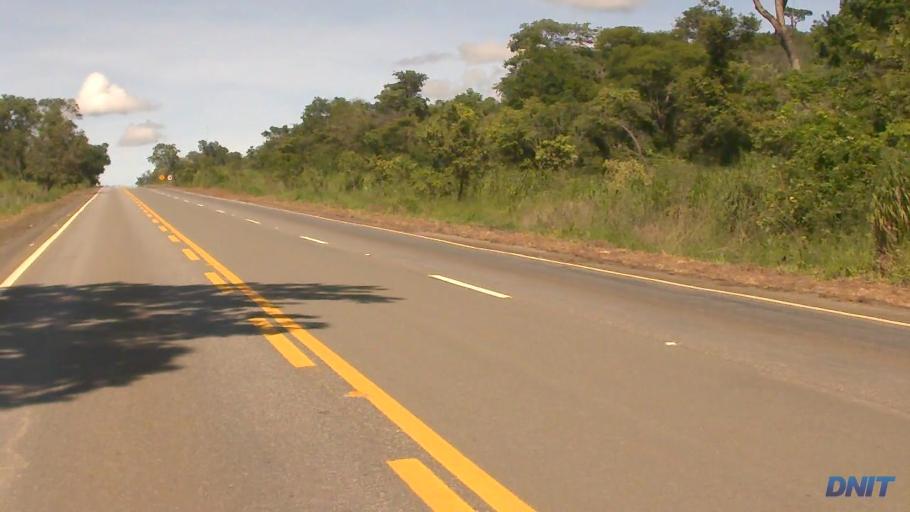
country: BR
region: Goias
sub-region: Padre Bernardo
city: Padre Bernardo
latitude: -15.2046
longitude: -48.4615
